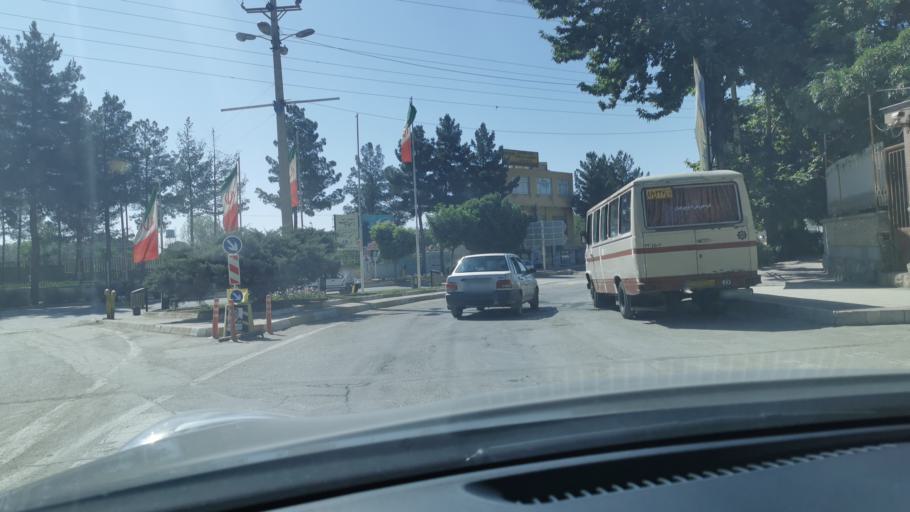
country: IR
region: Razavi Khorasan
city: Chenaran
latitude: 36.6418
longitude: 59.1181
